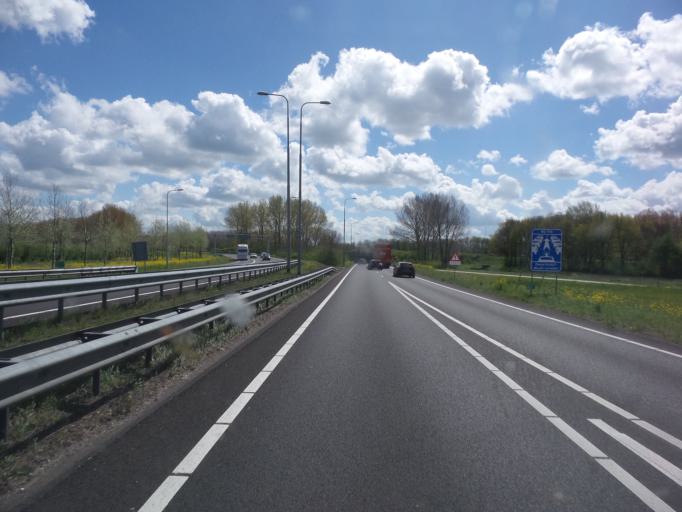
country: NL
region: South Holland
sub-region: Bodegraven-Reeuwijk
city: Bodegraven
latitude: 52.0685
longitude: 4.7441
